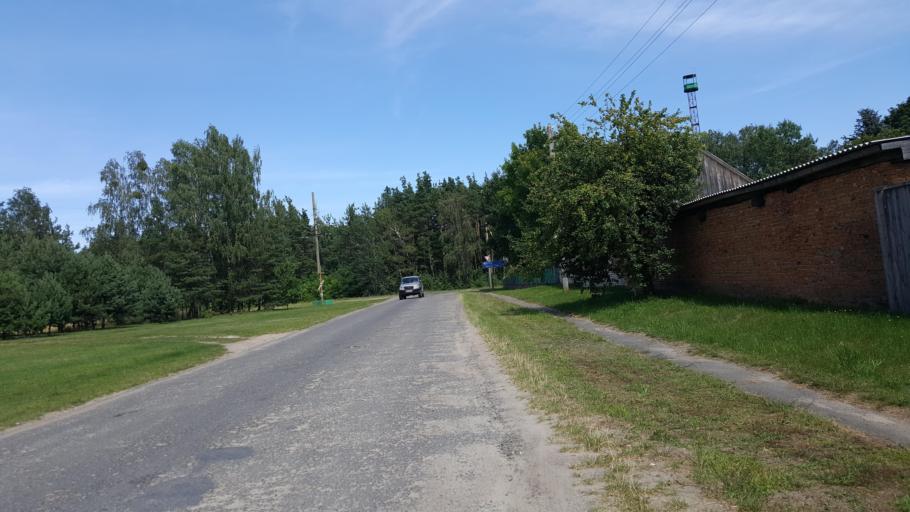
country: BY
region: Brest
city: Pruzhany
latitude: 52.5671
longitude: 24.2086
